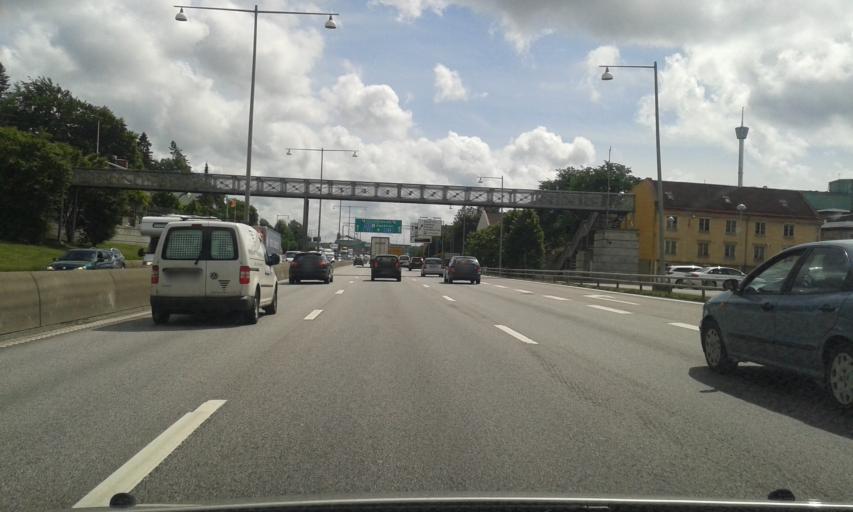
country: SE
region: Vaestra Goetaland
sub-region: Goteborg
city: Goeteborg
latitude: 57.7016
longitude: 11.9948
